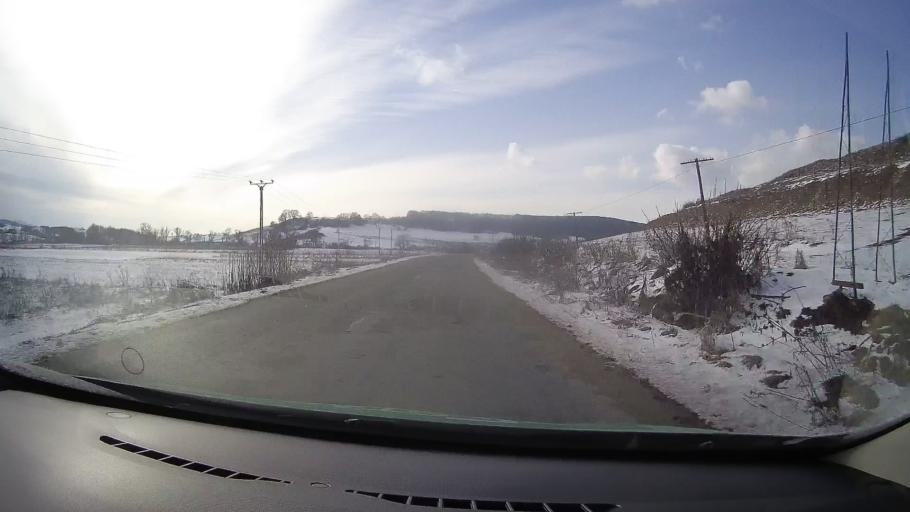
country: RO
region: Sibiu
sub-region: Comuna Iacobeni
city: Iacobeni
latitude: 46.0209
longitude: 24.7029
